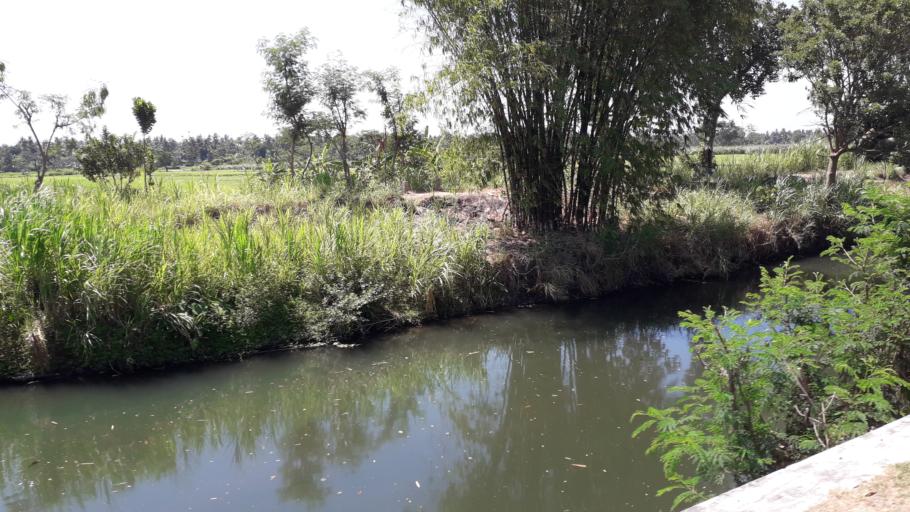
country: ID
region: Daerah Istimewa Yogyakarta
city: Pundong
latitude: -7.9478
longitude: 110.3287
